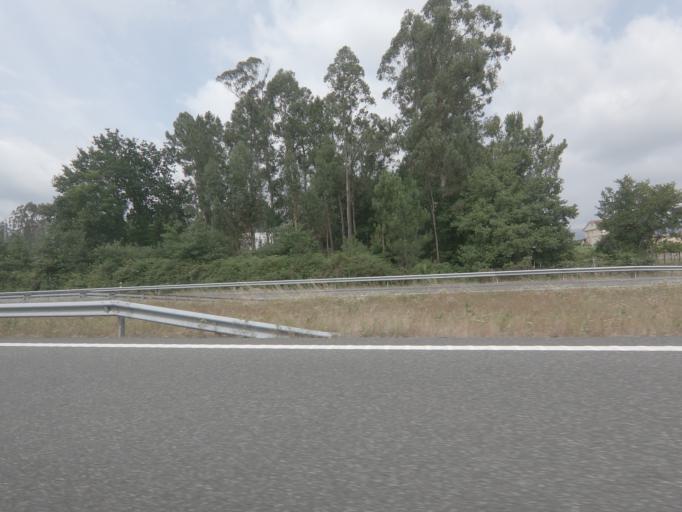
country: ES
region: Galicia
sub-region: Provincia de Pontevedra
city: Ponteareas
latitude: 42.1499
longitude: -8.4783
